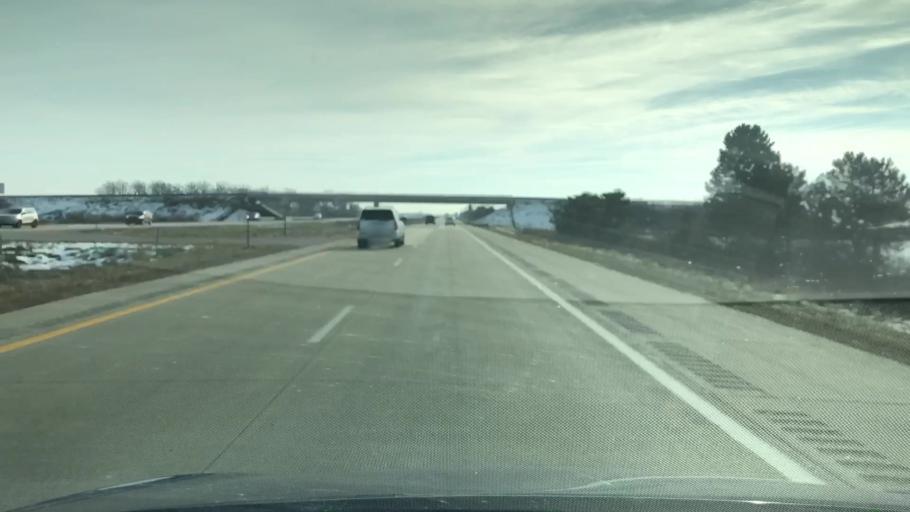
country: US
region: Michigan
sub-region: Bay County
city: Pinconning
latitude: 43.7697
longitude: -84.0224
